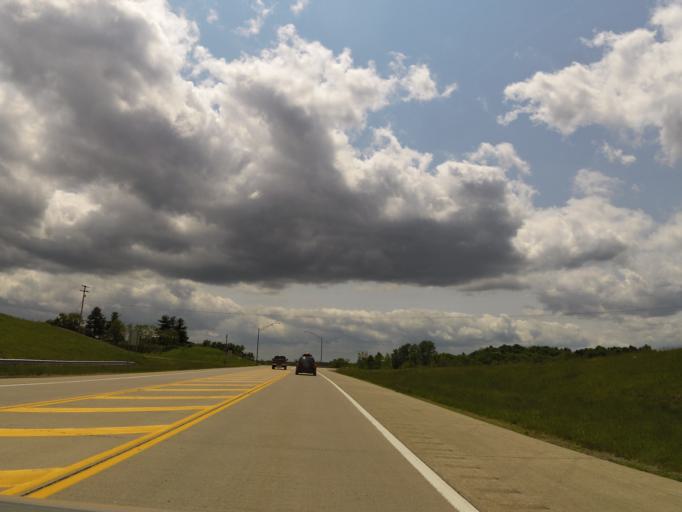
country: US
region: Ohio
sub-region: Athens County
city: Athens
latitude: 39.2003
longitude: -82.0552
